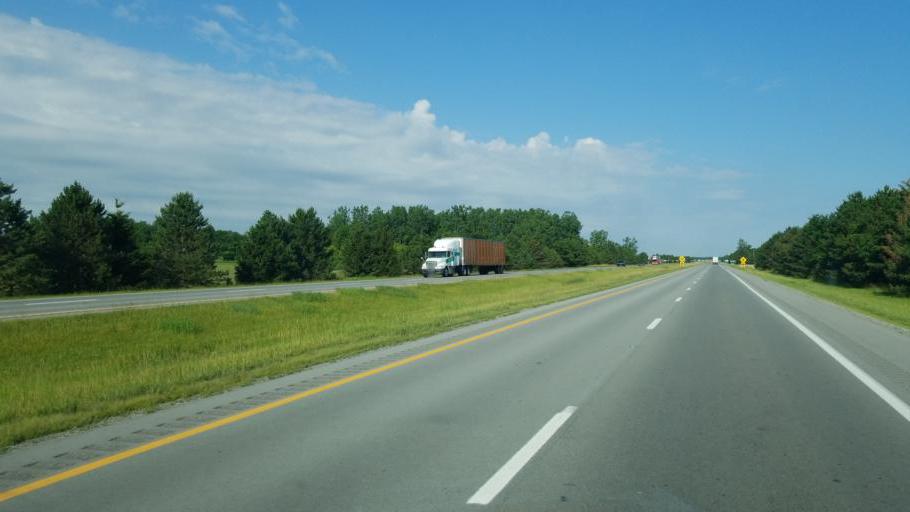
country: US
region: Ohio
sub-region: Hancock County
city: Findlay
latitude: 40.9862
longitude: -83.6064
